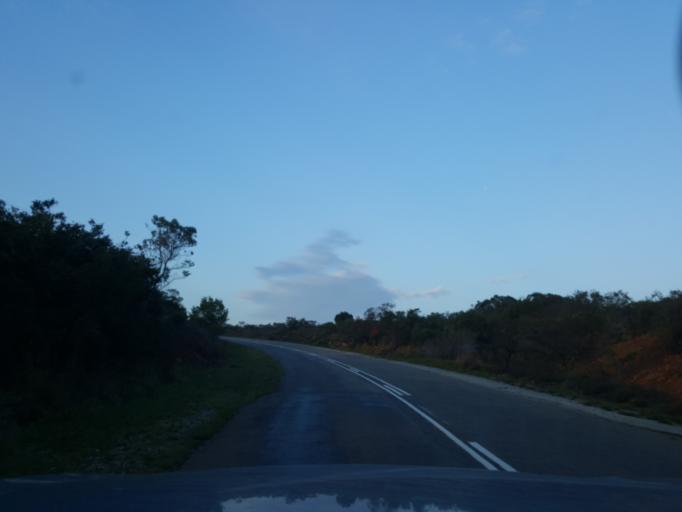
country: ZA
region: Eastern Cape
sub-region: Cacadu District Municipality
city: Grahamstown
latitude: -33.4622
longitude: 26.4937
